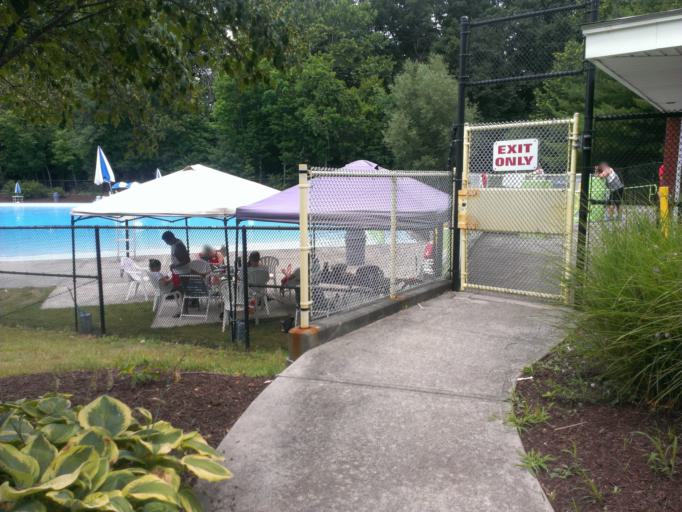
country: US
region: Connecticut
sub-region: New Haven County
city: Wallingford
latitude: 41.4722
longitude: -72.8083
